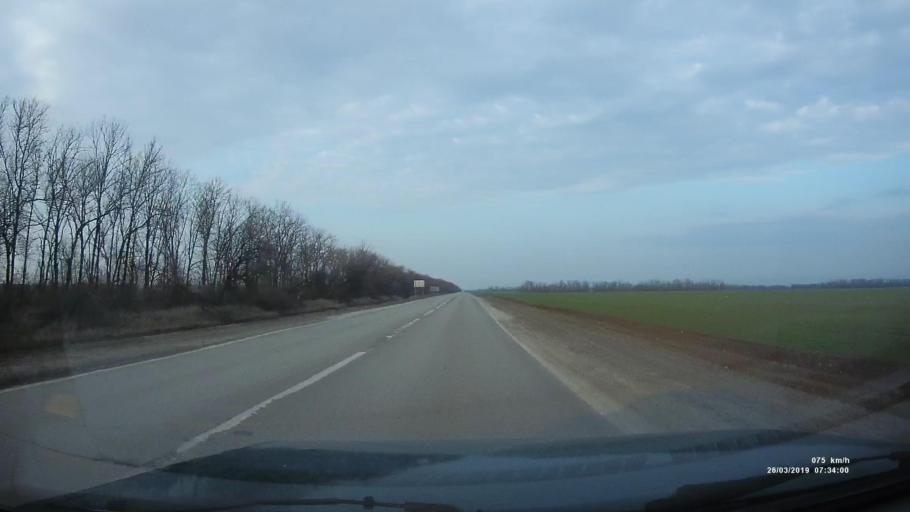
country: RU
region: Rostov
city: Novobessergenovka
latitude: 47.2116
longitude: 38.7650
